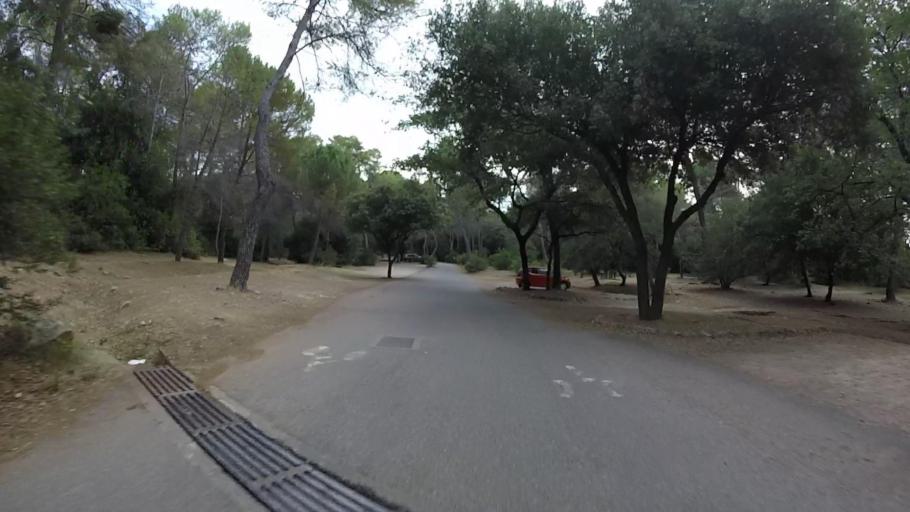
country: FR
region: Provence-Alpes-Cote d'Azur
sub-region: Departement des Alpes-Maritimes
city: Vallauris
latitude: 43.6062
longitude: 7.0408
